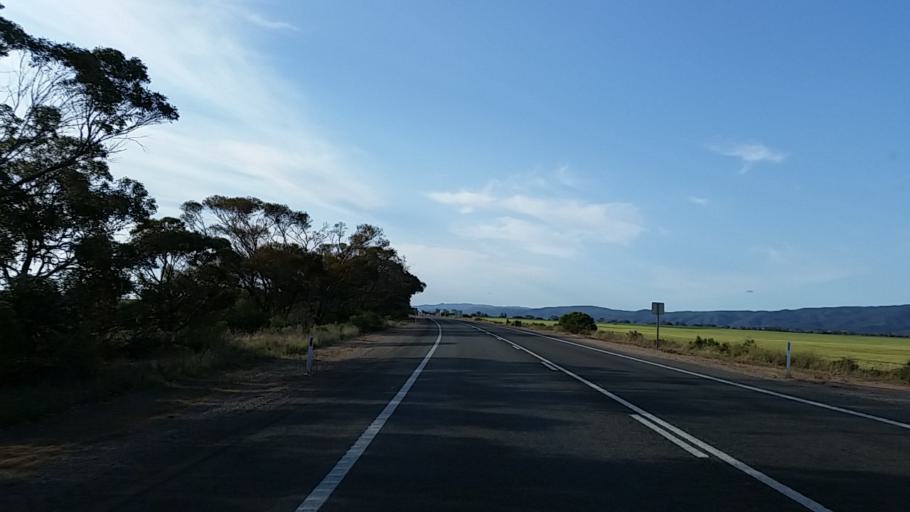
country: AU
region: South Australia
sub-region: Port Pirie City and Dists
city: Solomontown
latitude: -33.1557
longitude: 138.0683
